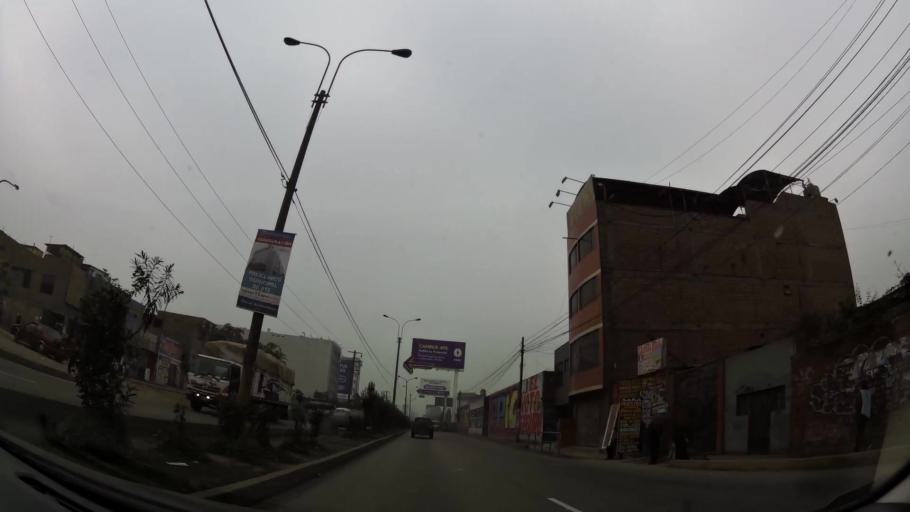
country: PE
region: Lima
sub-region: Lima
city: Vitarte
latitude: -12.0232
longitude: -76.9115
